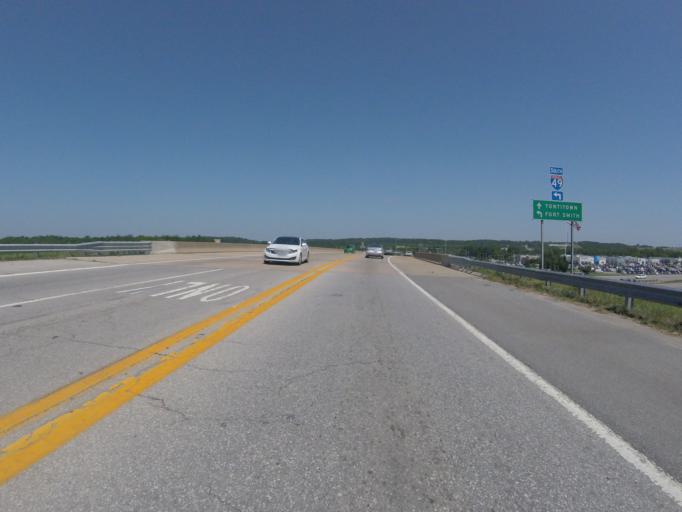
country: US
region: Arkansas
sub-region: Washington County
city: Johnson
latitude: 36.1051
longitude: -94.1797
